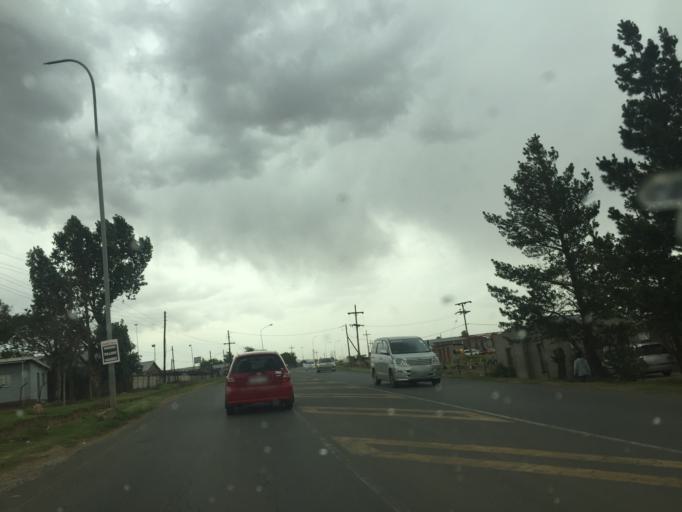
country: LS
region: Maseru
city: Maseru
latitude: -29.2835
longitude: 27.5276
